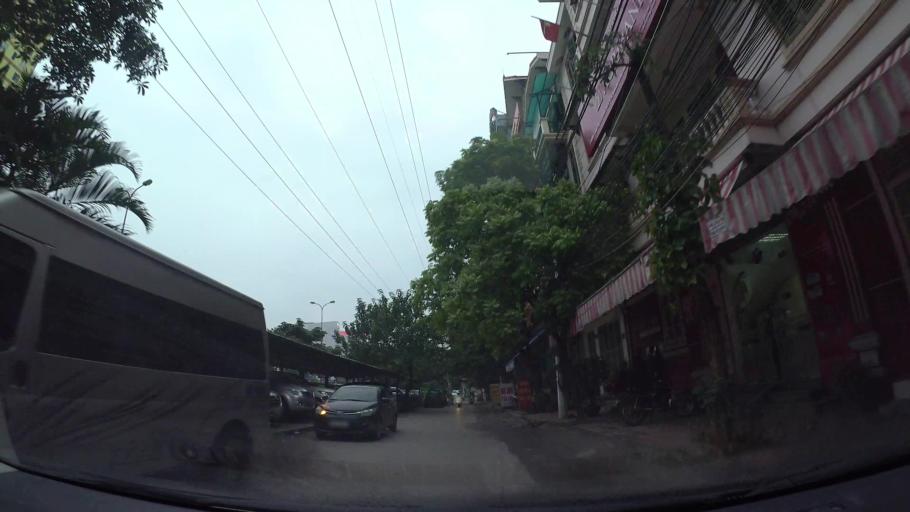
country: VN
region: Ha Noi
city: Hai BaTrung
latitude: 21.0122
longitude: 105.8640
